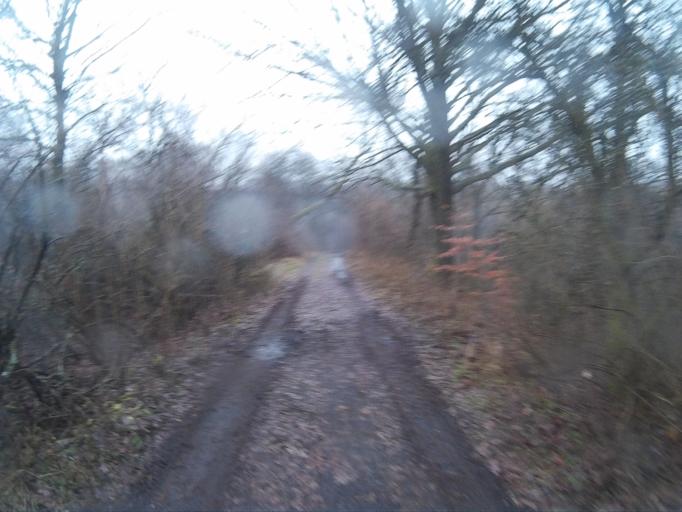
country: HU
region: Nograd
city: Somoskoujfalu
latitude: 48.1625
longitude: 19.8566
